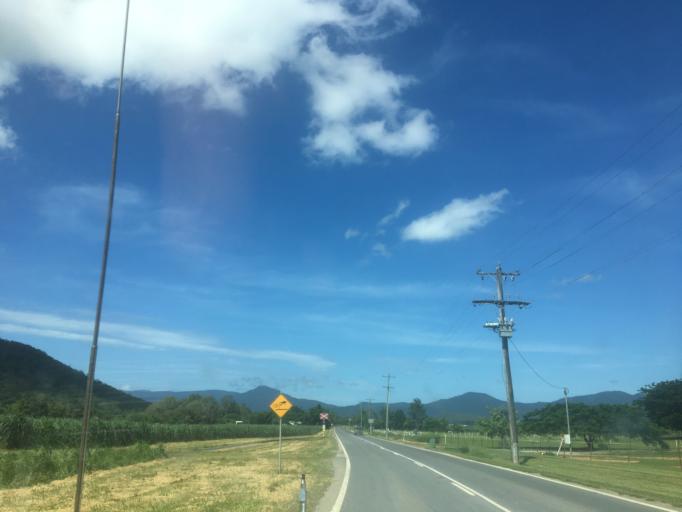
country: AU
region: Queensland
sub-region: Cairns
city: Woree
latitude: -17.0670
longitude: 145.7518
